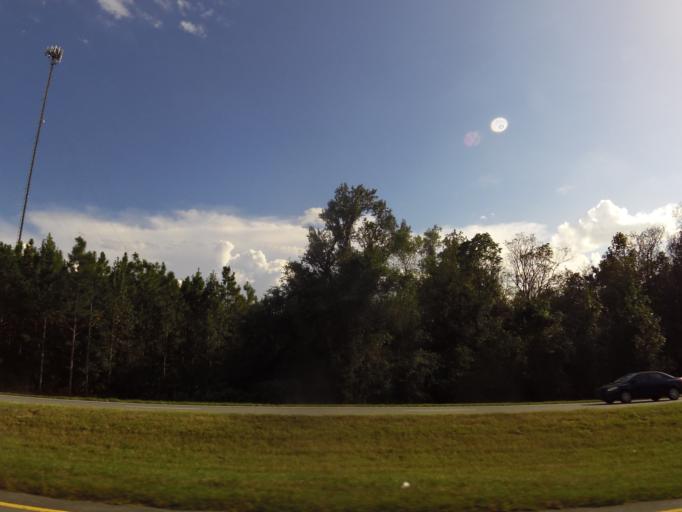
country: US
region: Georgia
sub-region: Brooks County
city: Quitman
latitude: 30.7854
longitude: -83.6092
